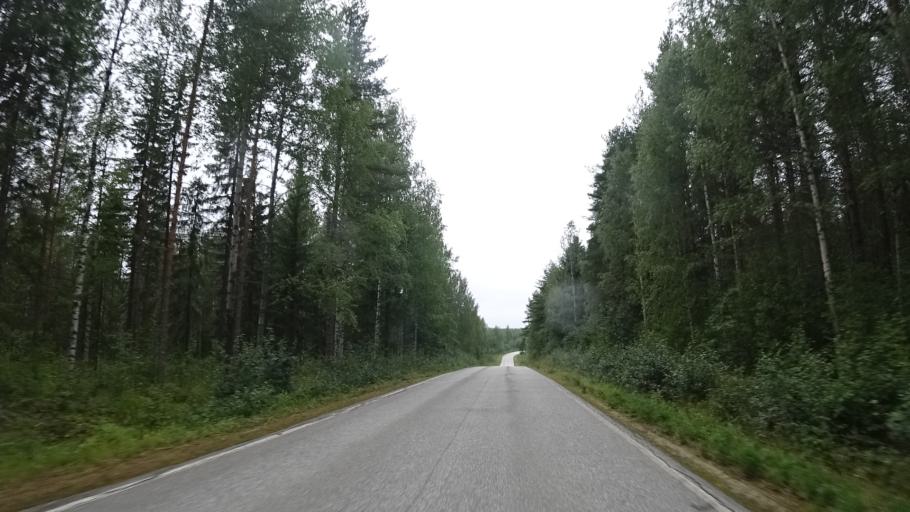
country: FI
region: North Karelia
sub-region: Pielisen Karjala
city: Lieksa
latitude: 63.3230
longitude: 30.2179
